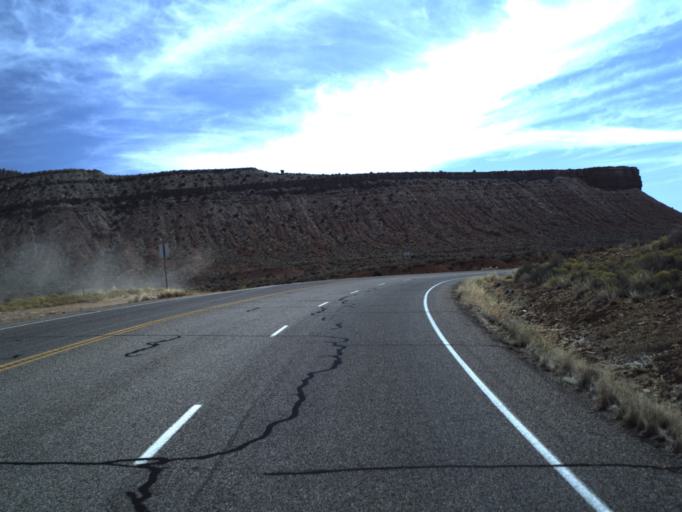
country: US
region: Utah
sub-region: Washington County
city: LaVerkin
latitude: 37.2267
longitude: -113.2537
